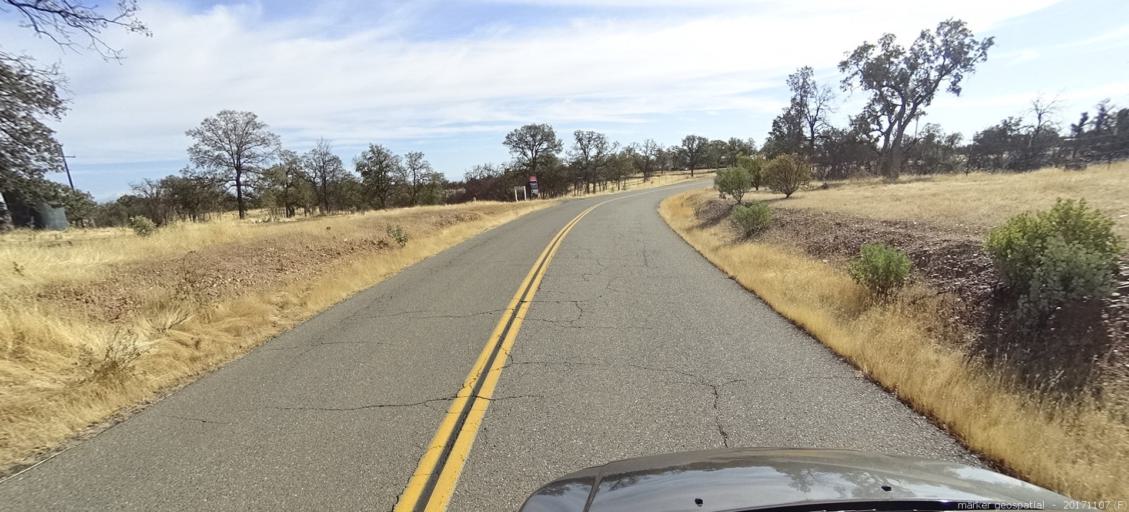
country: US
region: California
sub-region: Shasta County
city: Shasta
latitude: 40.4622
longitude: -122.5368
